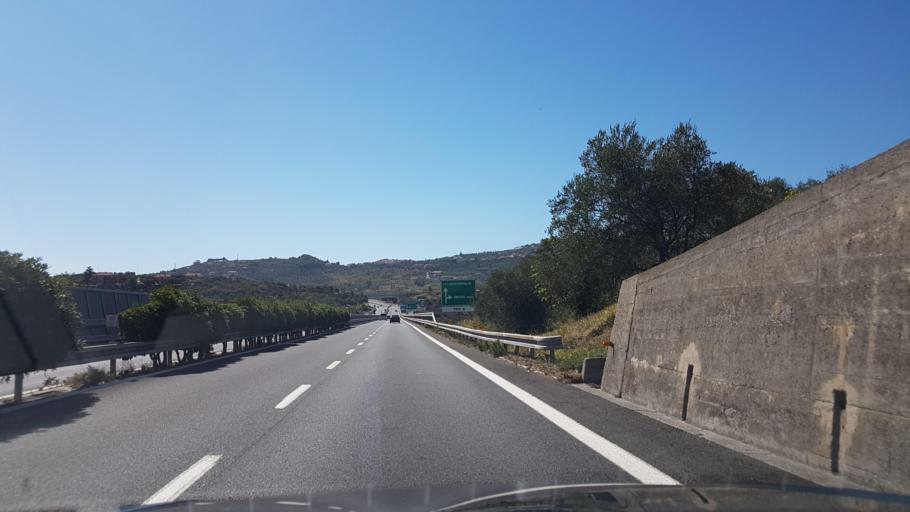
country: IT
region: Liguria
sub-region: Provincia di Imperia
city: Imperia
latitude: 43.8822
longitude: 8.0038
